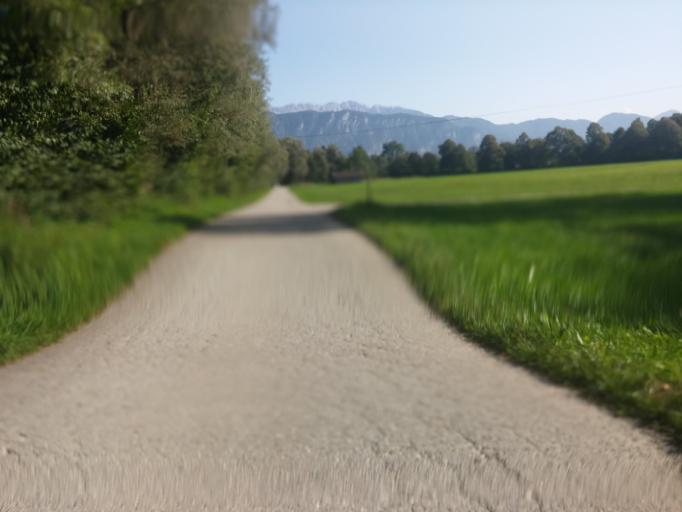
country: DE
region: Bavaria
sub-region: Upper Bavaria
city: Oberaudorf
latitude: 47.6498
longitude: 12.1913
